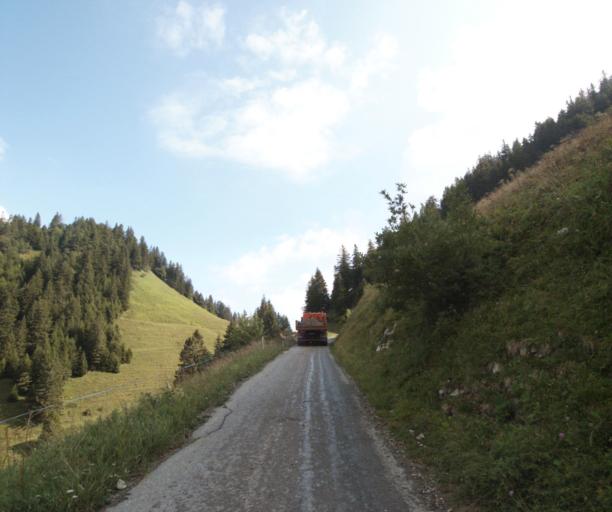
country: CH
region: Vaud
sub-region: Riviera-Pays-d'Enhaut District
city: Caux
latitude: 46.4201
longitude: 6.9959
